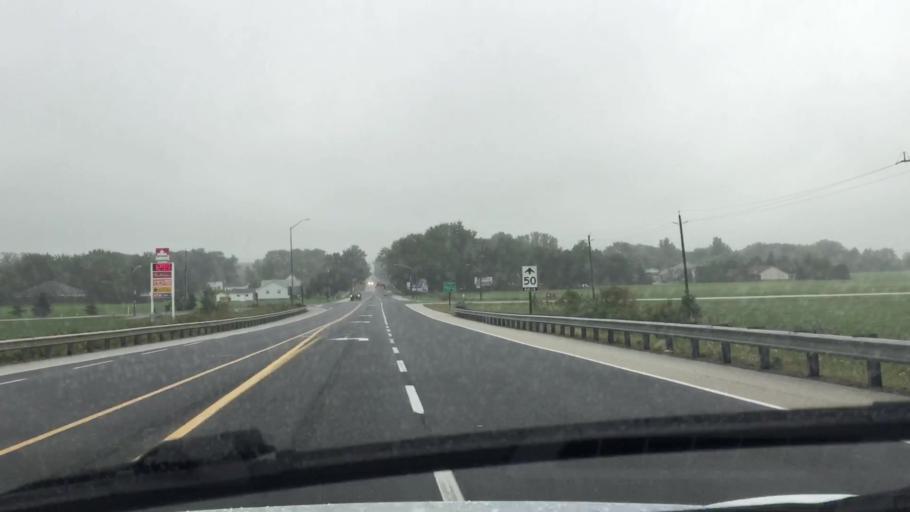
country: CA
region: Ontario
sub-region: Lambton County
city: Walpole Island
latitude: 42.2399
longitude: -82.5523
